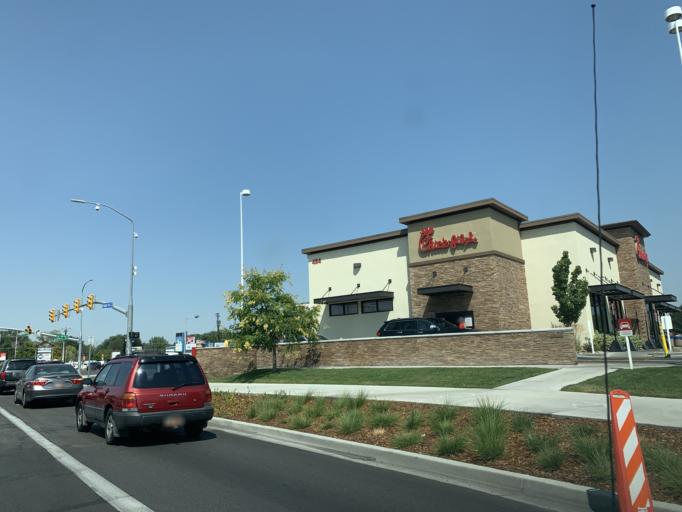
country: US
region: Utah
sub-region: Utah County
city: Provo
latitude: 40.2507
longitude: -111.6668
